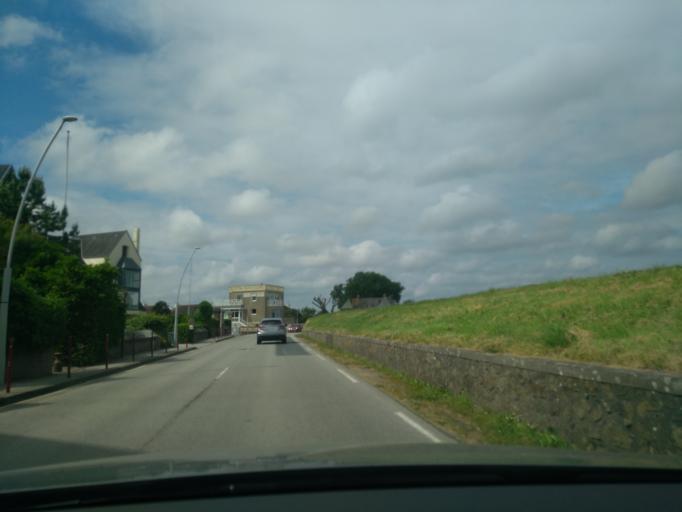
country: FR
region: Lower Normandy
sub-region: Departement de la Manche
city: Saint-Vaast-la-Hougue
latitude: 49.5921
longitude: -1.2668
